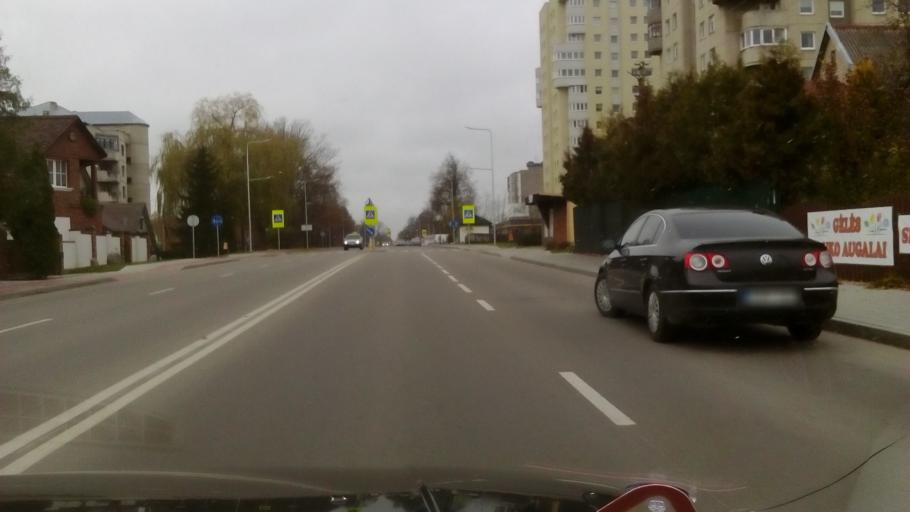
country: LT
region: Marijampoles apskritis
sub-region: Marijampole Municipality
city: Marijampole
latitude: 54.5620
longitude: 23.3360
